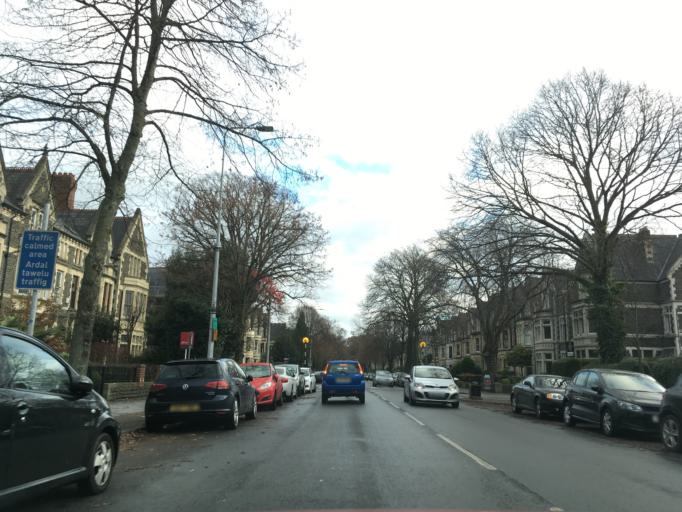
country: GB
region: Wales
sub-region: Cardiff
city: Cardiff
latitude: 51.4877
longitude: -3.1982
